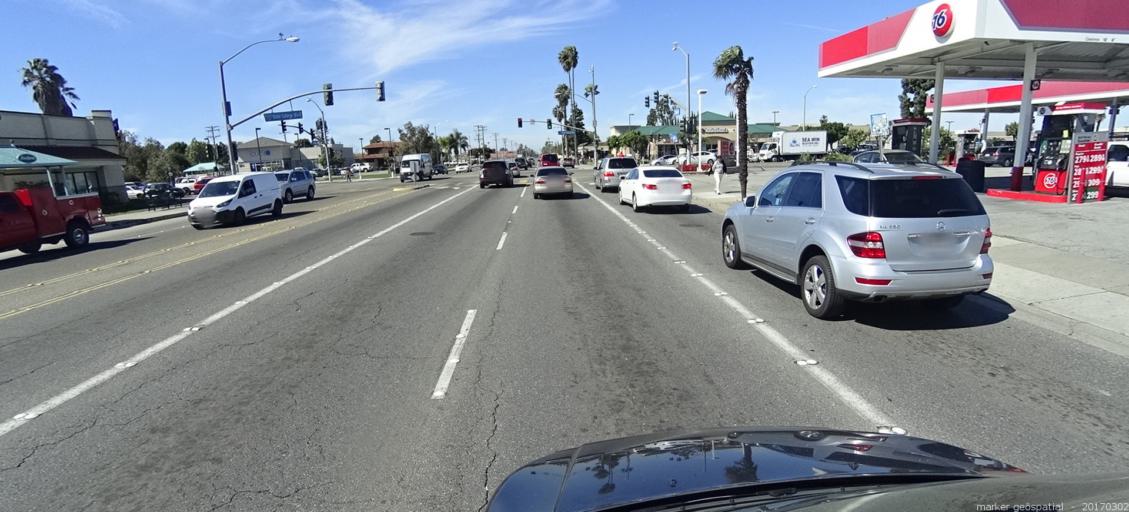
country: US
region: California
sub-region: Orange County
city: Anaheim
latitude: 33.8473
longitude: -117.8885
